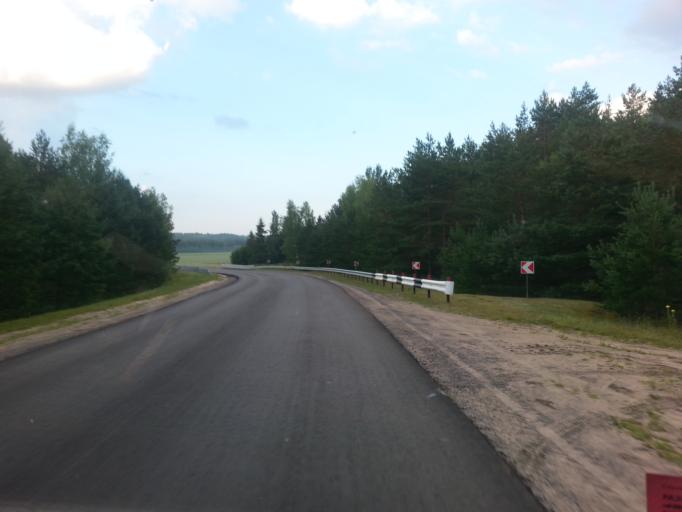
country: BY
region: Minsk
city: Il'ya
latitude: 54.5398
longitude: 27.2077
